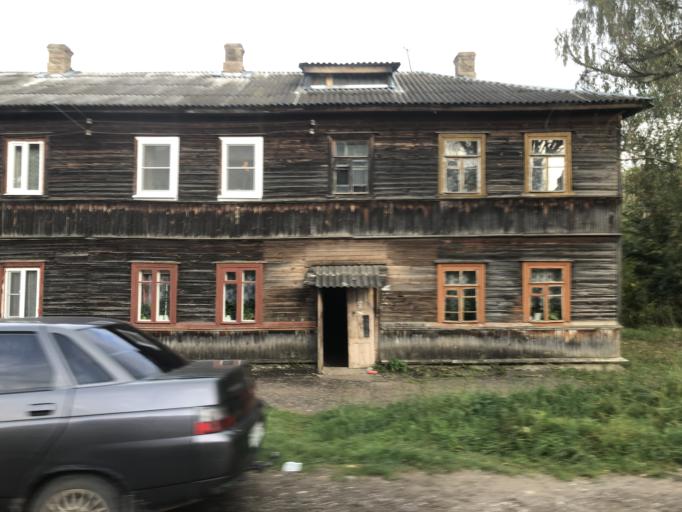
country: RU
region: Tverskaya
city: Rzhev
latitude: 56.2547
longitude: 34.2930
